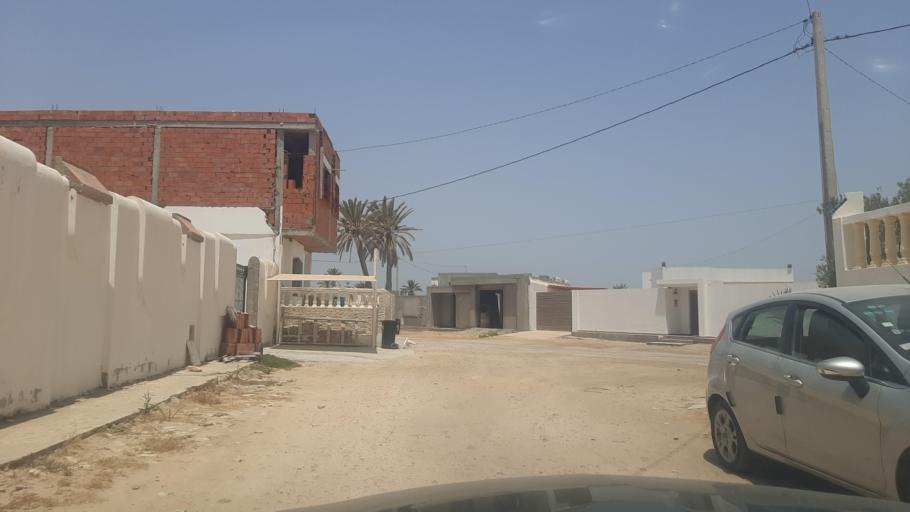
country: TN
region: Safaqis
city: Al Qarmadah
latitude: 34.7048
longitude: 11.1953
